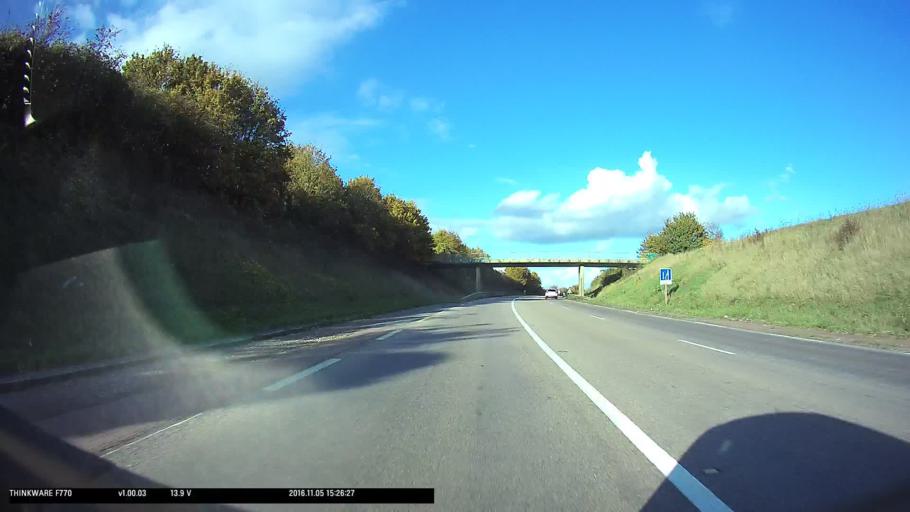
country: FR
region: Ile-de-France
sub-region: Departement des Yvelines
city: Meulan-en-Yvelines
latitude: 49.0237
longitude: 1.9100
